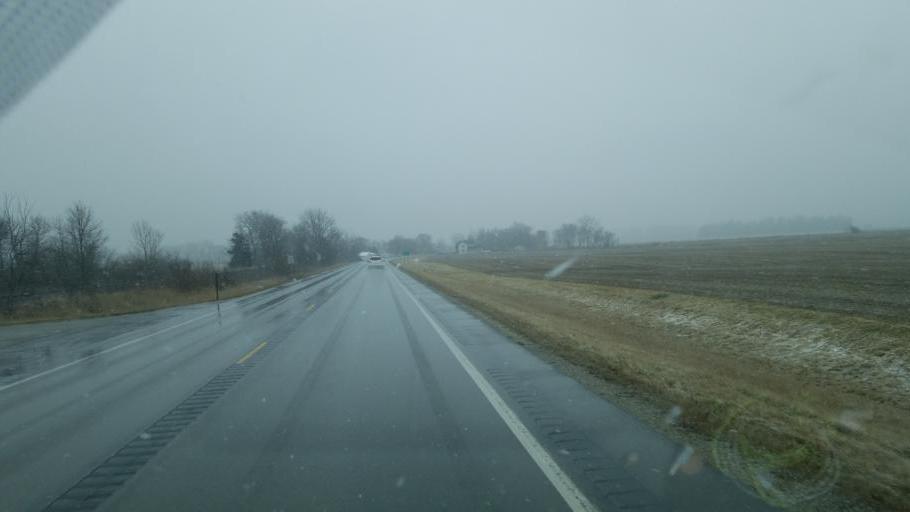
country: US
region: Indiana
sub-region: Grant County
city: Sweetser
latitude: 40.6648
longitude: -85.7181
